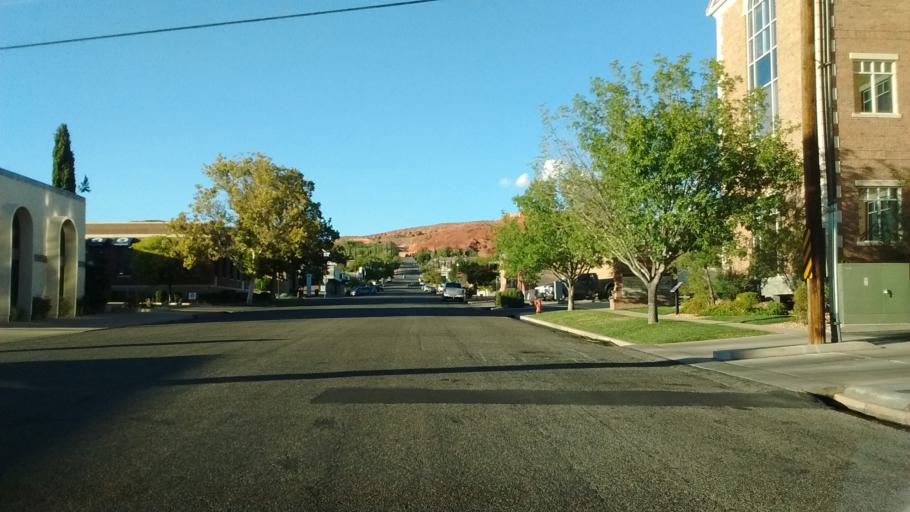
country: US
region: Utah
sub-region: Washington County
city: Saint George
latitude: 37.1072
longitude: -113.5812
